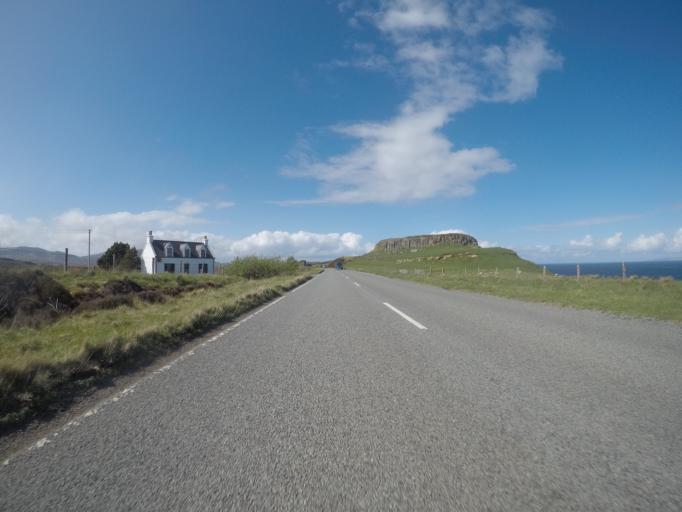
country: GB
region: Scotland
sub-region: Highland
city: Portree
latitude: 57.5981
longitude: -6.1628
